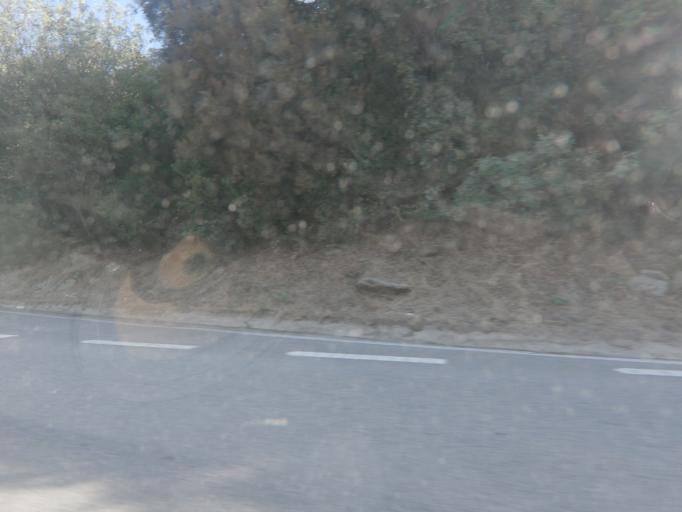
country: PT
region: Viseu
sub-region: Tabuaco
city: Tabuaco
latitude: 41.1585
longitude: -7.6091
